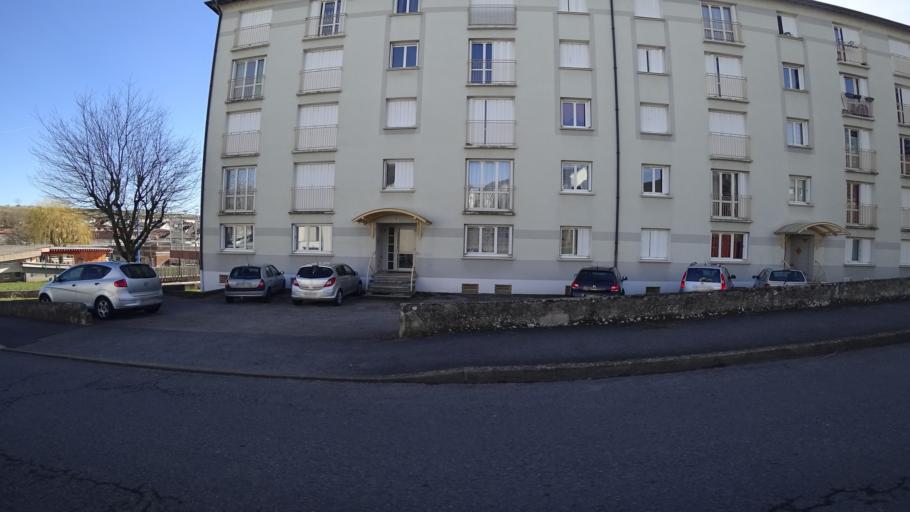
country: FR
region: Midi-Pyrenees
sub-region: Departement de l'Aveyron
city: Rodez
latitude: 44.3655
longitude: 2.5944
